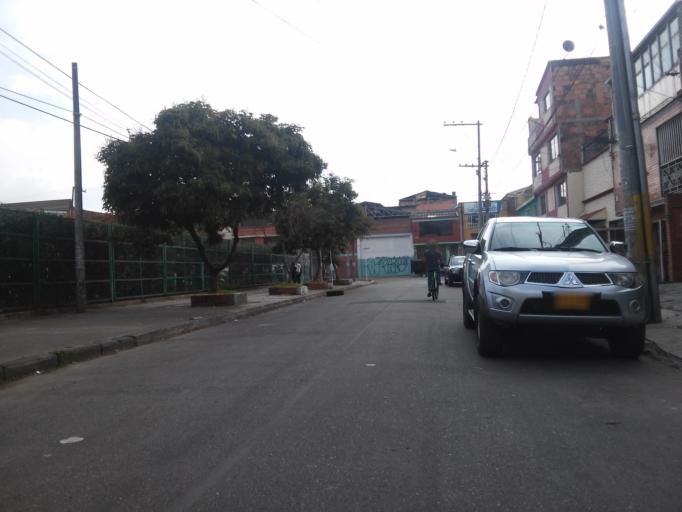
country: CO
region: Bogota D.C.
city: Bogota
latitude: 4.6186
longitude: -74.1422
